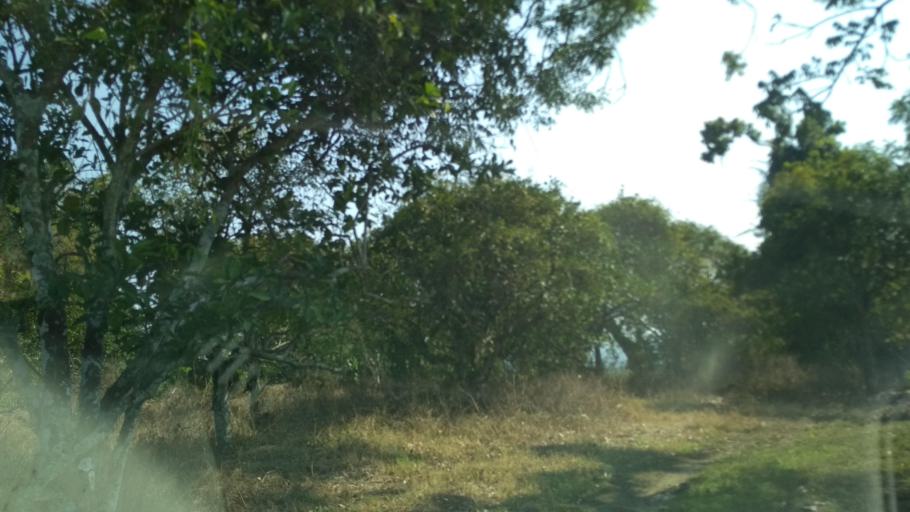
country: MX
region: Puebla
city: San Jose Acateno
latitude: 20.1935
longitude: -97.1858
